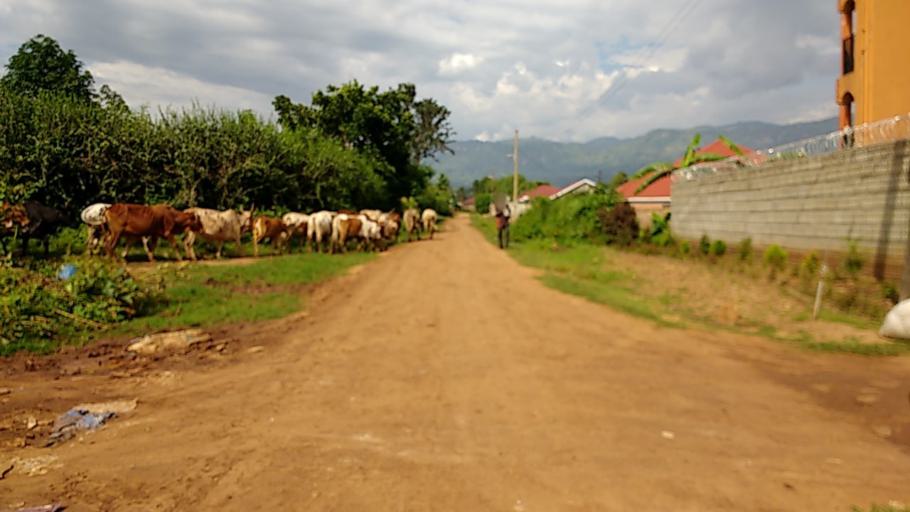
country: UG
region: Eastern Region
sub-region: Mbale District
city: Mbale
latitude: 1.0662
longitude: 34.1672
